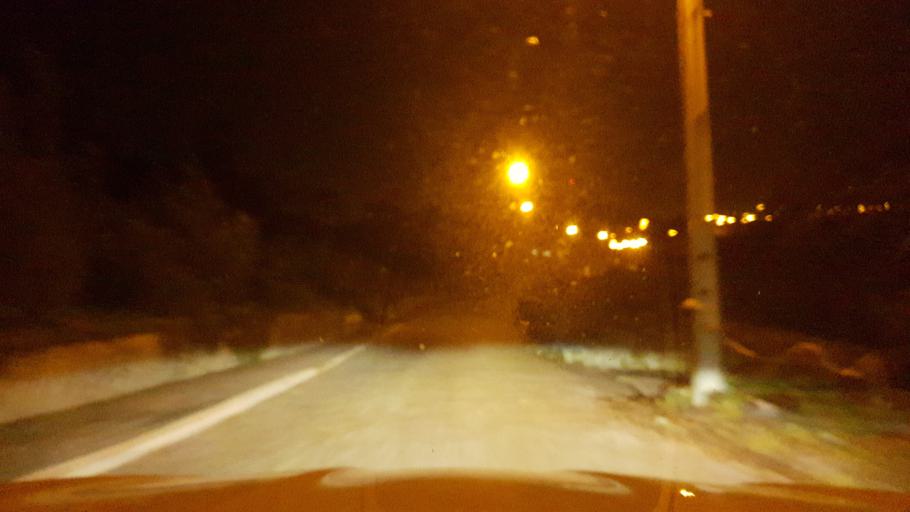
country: PT
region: Porto
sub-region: Matosinhos
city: Guifoes
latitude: 41.2183
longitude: -8.6613
